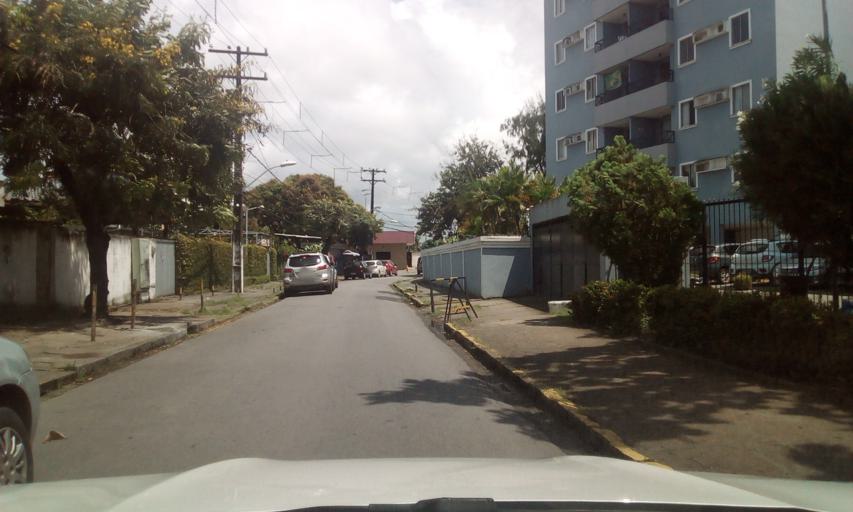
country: BR
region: Pernambuco
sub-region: Recife
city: Recife
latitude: -8.0601
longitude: -34.9272
